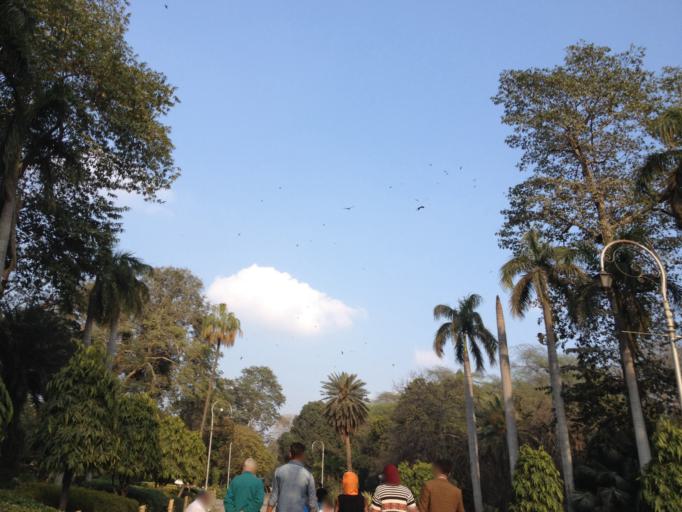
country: PK
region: Punjab
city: Lahore
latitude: 31.5544
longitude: 74.3269
